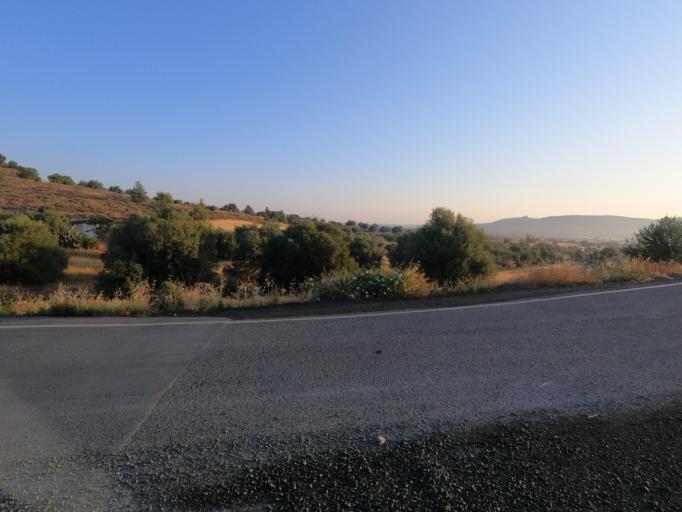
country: CY
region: Lefkosia
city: Alampra
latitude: 34.9903
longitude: 33.3912
